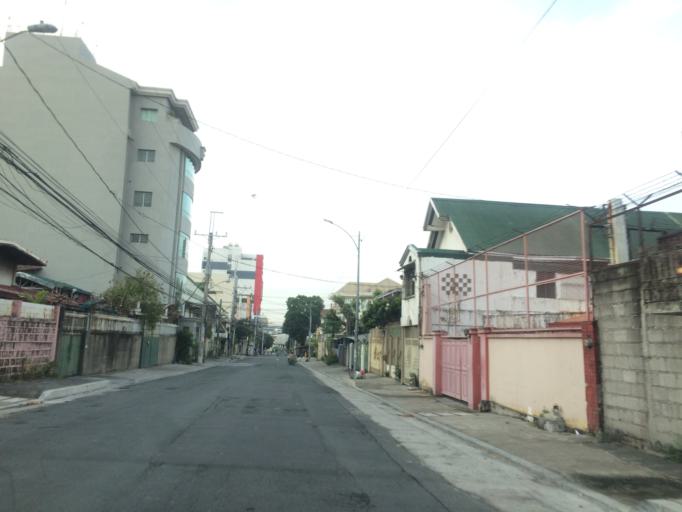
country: PH
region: Calabarzon
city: Del Monte
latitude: 14.6366
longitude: 121.0037
